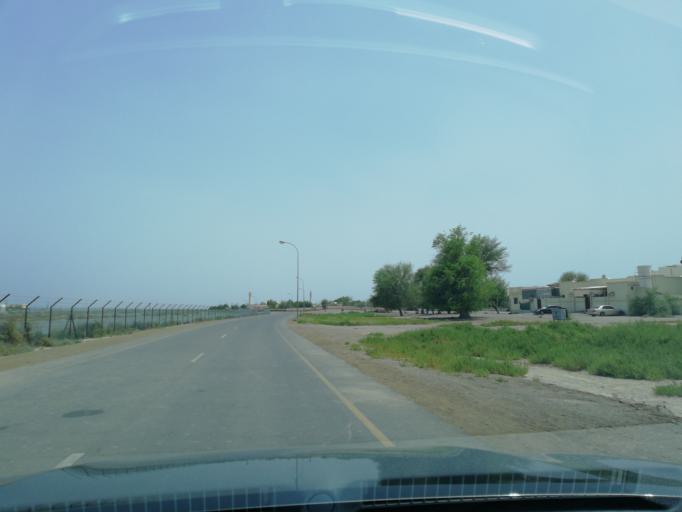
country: OM
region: Al Batinah
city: Shinas
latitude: 24.7500
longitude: 56.4675
